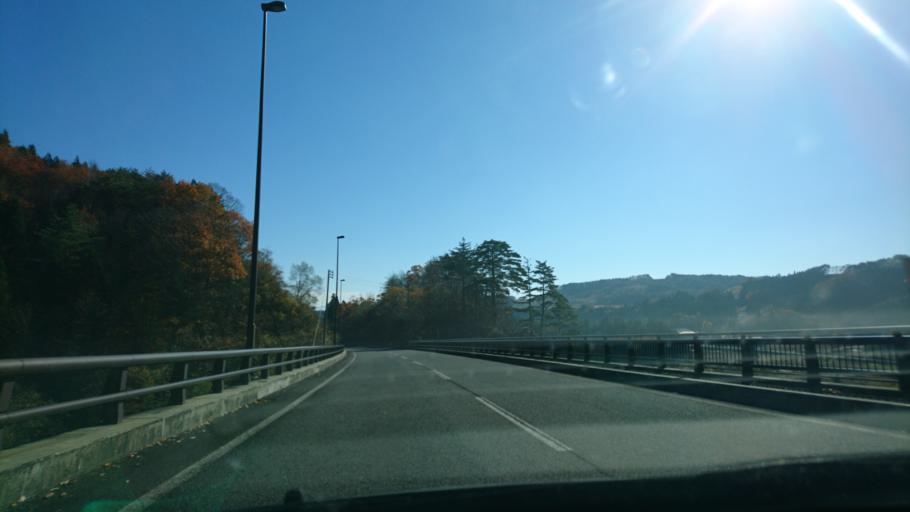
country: JP
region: Iwate
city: Mizusawa
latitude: 39.1218
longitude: 140.9394
